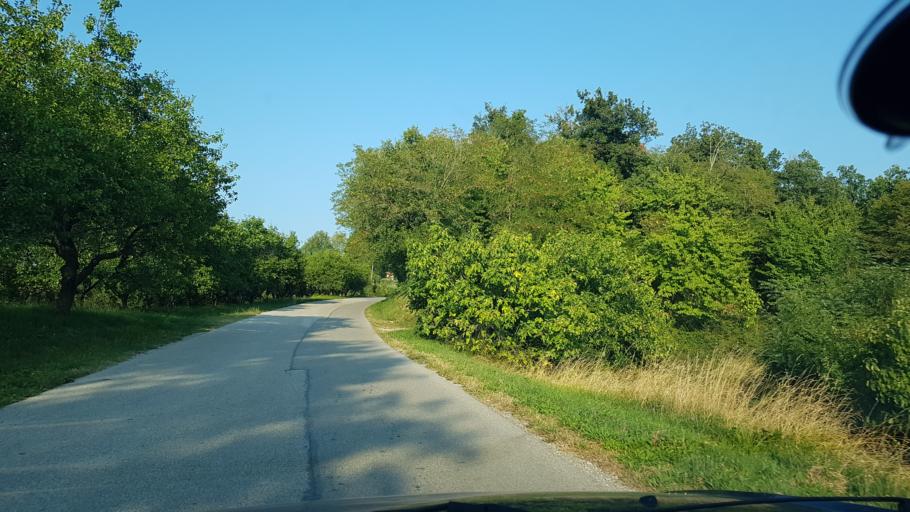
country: IT
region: Friuli Venezia Giulia
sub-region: Provincia di Gorizia
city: San Floriano del Collio
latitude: 45.9868
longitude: 13.5759
